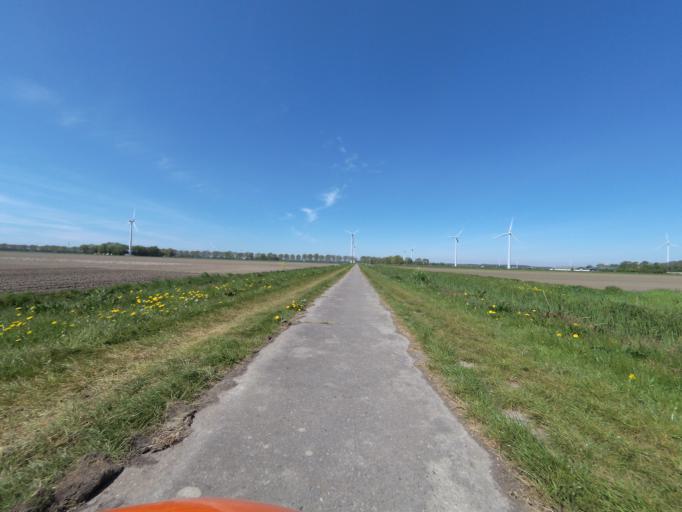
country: NL
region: Flevoland
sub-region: Gemeente Zeewolde
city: Zeewolde
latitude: 52.3730
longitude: 5.5142
